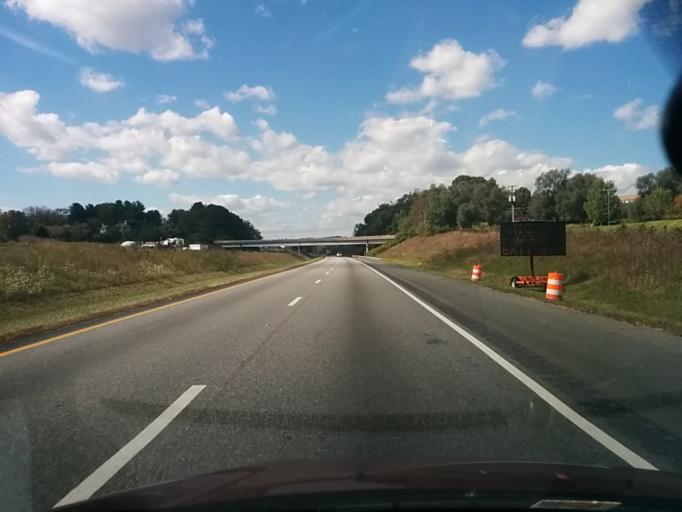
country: US
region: Virginia
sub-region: City of Waynesboro
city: Waynesboro
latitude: 38.0525
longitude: -78.9161
